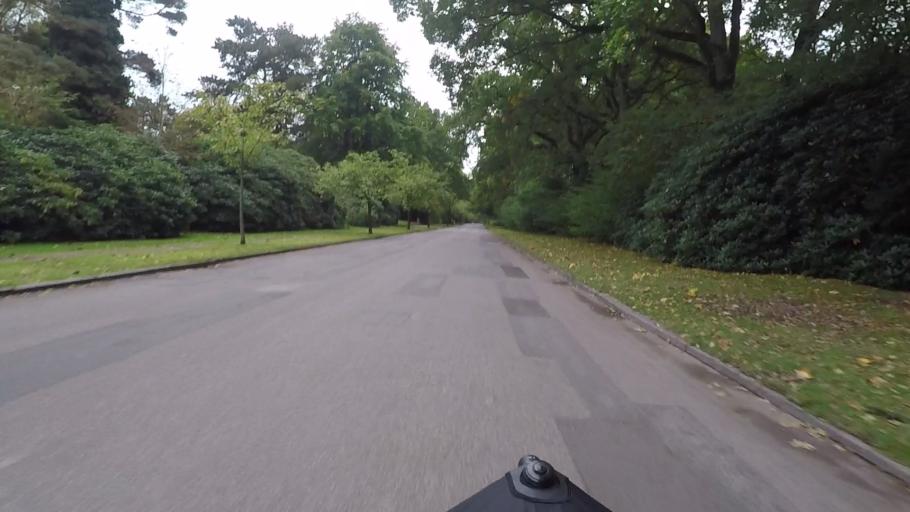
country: DE
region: Hamburg
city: Wellingsbuettel
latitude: 53.6266
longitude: 10.0732
